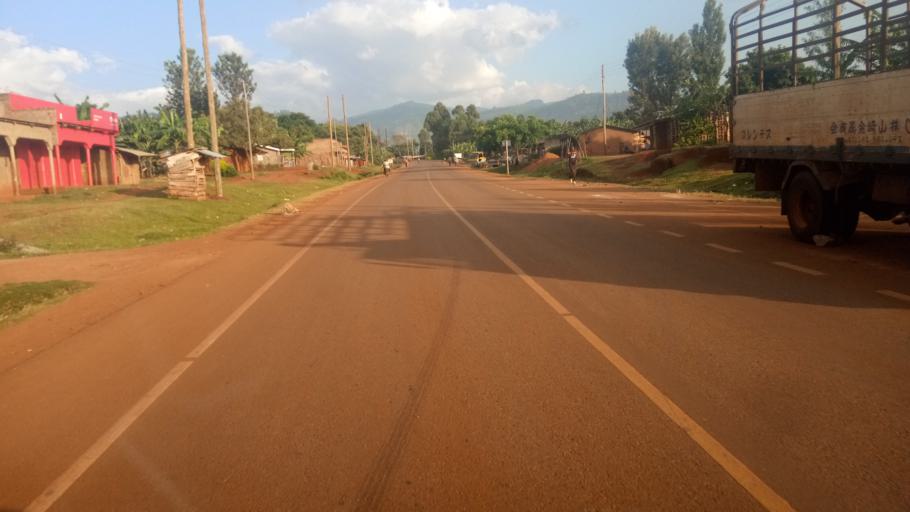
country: UG
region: Eastern Region
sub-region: Sironko District
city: Sironko
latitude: 1.3210
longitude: 34.3368
